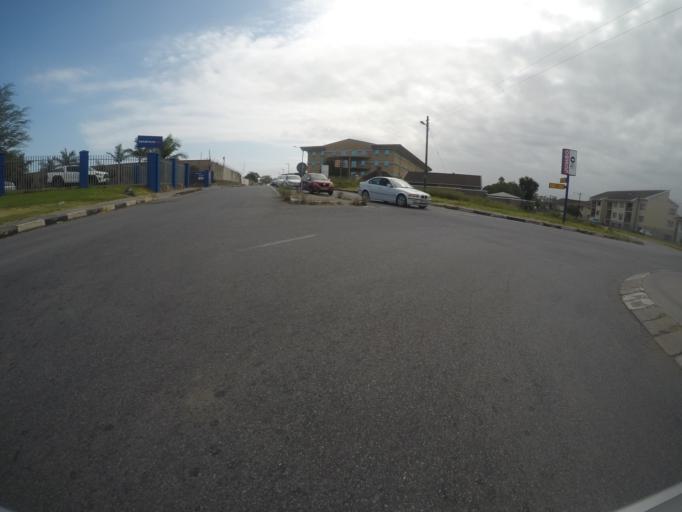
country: ZA
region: Eastern Cape
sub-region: Buffalo City Metropolitan Municipality
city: East London
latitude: -32.9835
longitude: 27.8956
